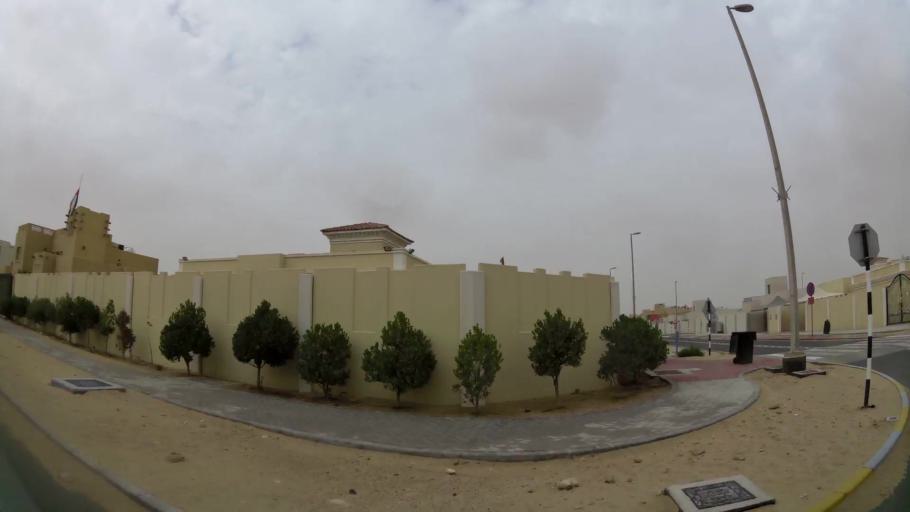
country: AE
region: Abu Dhabi
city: Abu Dhabi
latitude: 24.4561
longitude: 54.7348
